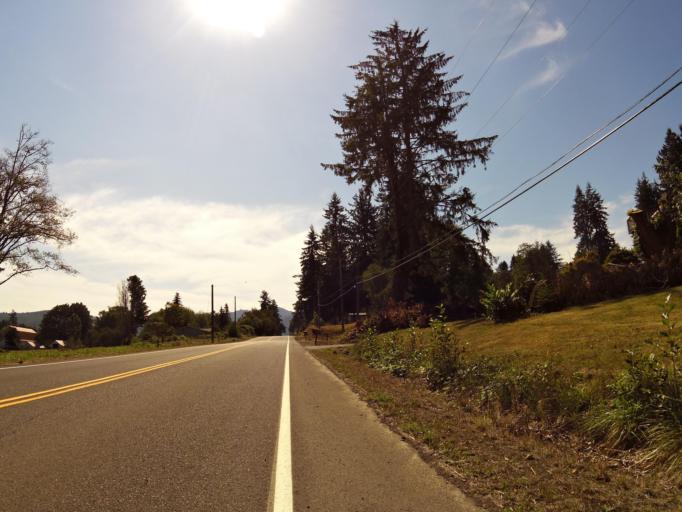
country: US
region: Washington
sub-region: Wahkiakum County
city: Cathlamet
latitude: 46.1789
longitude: -123.5830
